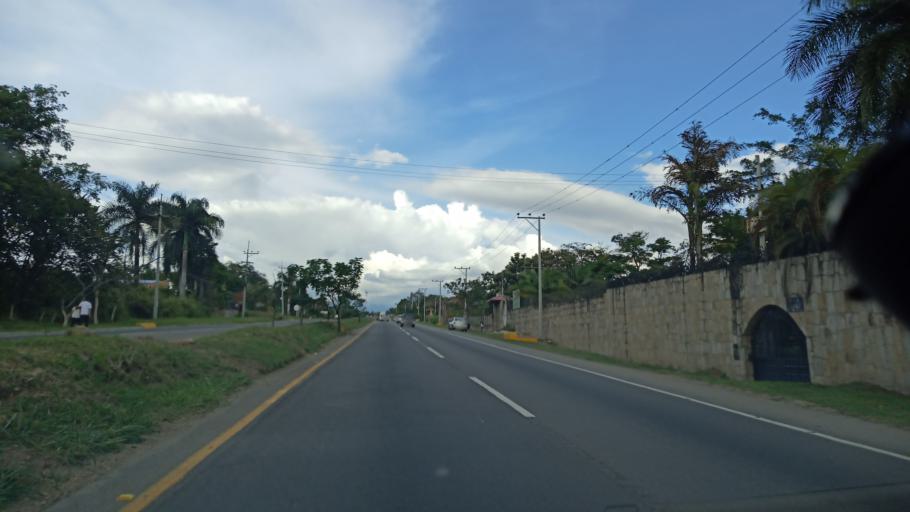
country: CO
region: Cundinamarca
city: Arbelaez
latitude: 4.2912
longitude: -74.4636
